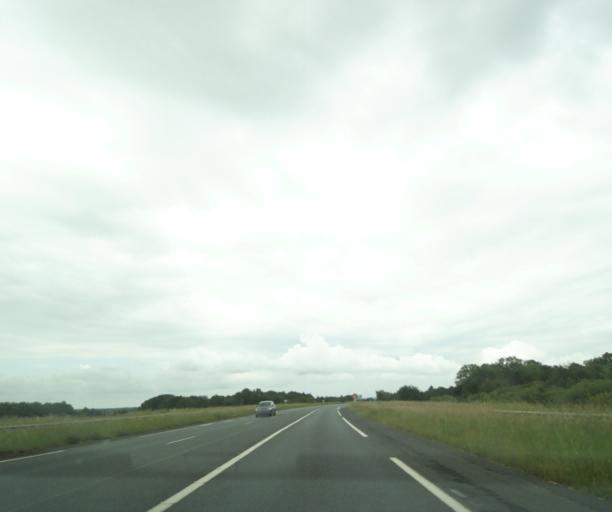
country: FR
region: Poitou-Charentes
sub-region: Departement des Deux-Sevres
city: Saint-Varent
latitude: 46.8648
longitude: -0.2071
